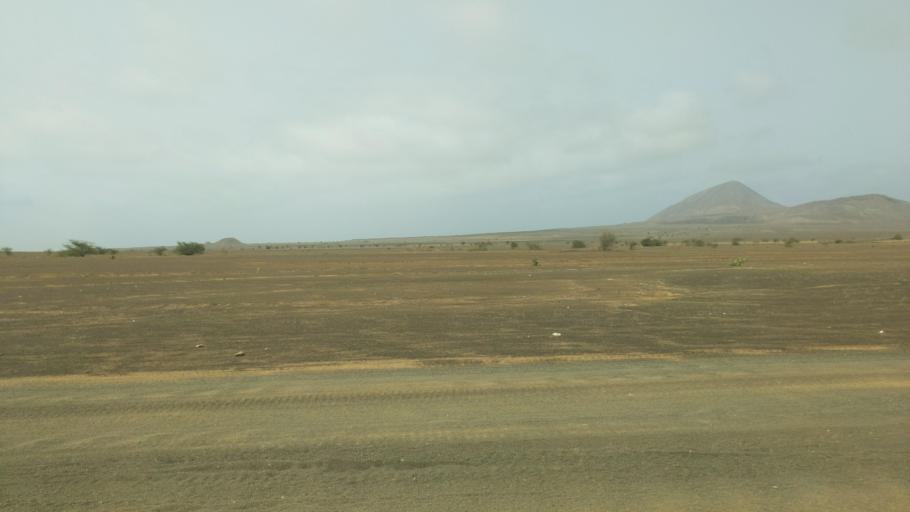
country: CV
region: Sal
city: Espargos
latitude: 16.7980
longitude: -22.9578
